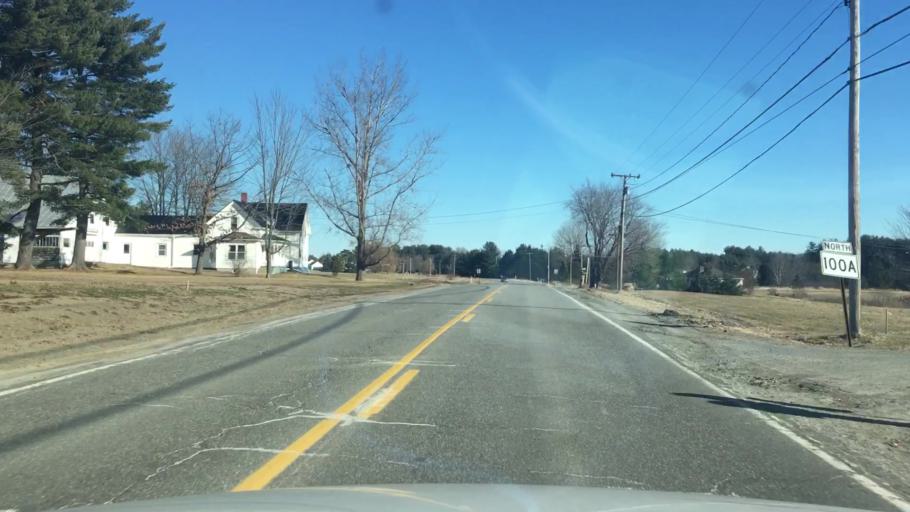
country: US
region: Maine
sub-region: Kennebec County
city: Winslow
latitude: 44.5479
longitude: -69.5952
